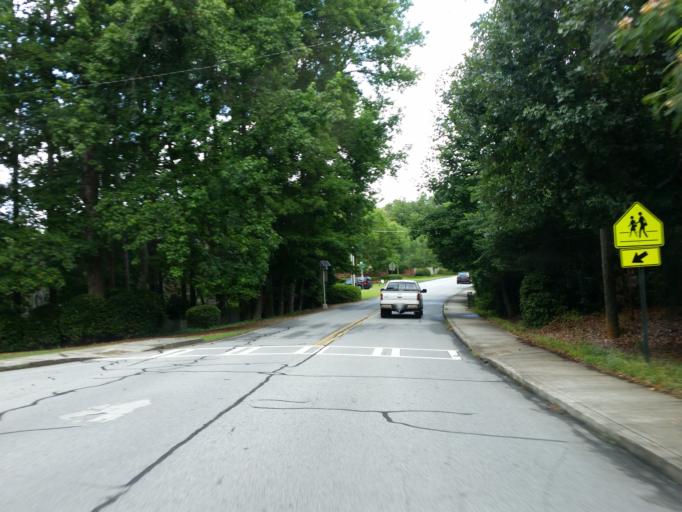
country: US
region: Georgia
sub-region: DeKalb County
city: Dunwoody
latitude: 33.9599
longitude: -84.3449
